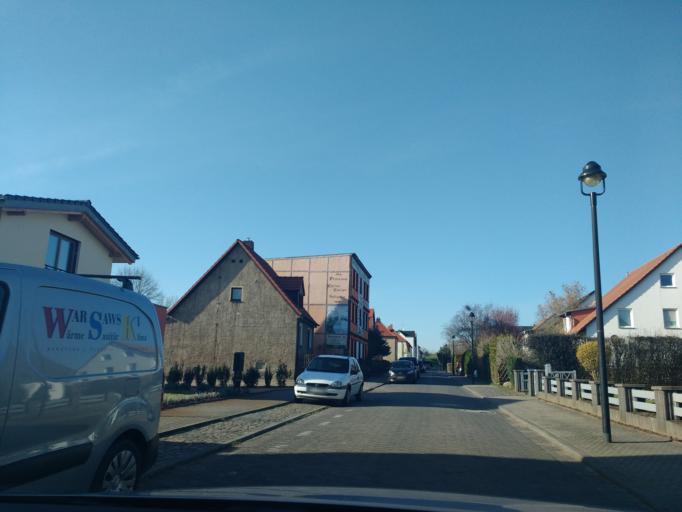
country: DE
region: Saxony-Anhalt
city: Gutenberg
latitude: 51.5322
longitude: 11.9739
